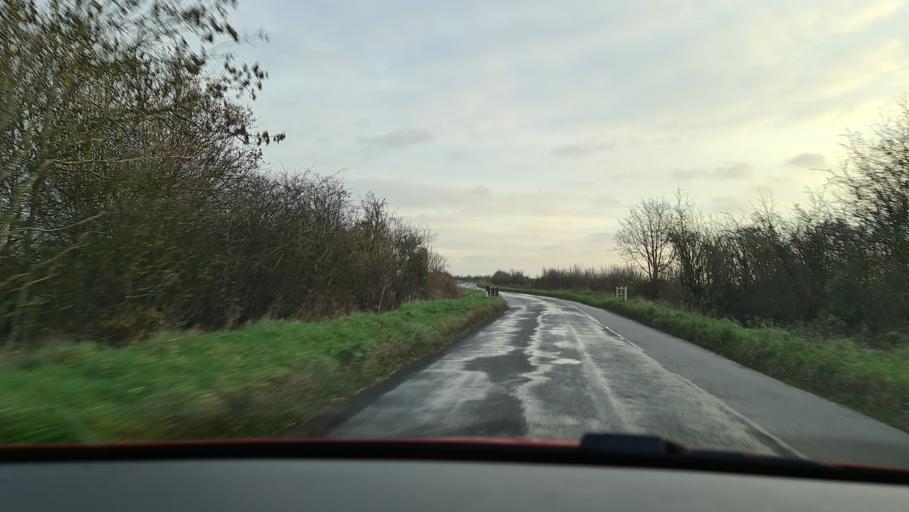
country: GB
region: England
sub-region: Oxfordshire
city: Kidlington
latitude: 51.8264
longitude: -1.2231
